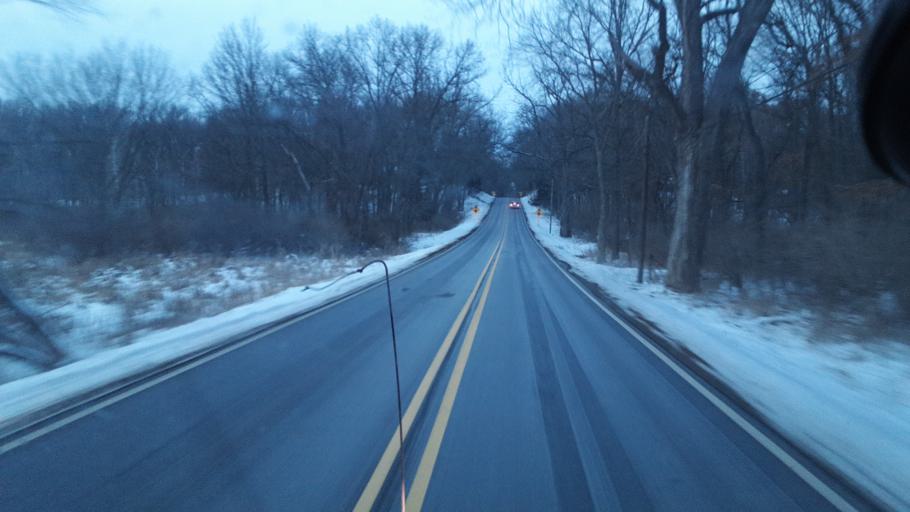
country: US
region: Michigan
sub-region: Jackson County
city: Grass Lake
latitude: 42.3217
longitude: -84.2096
